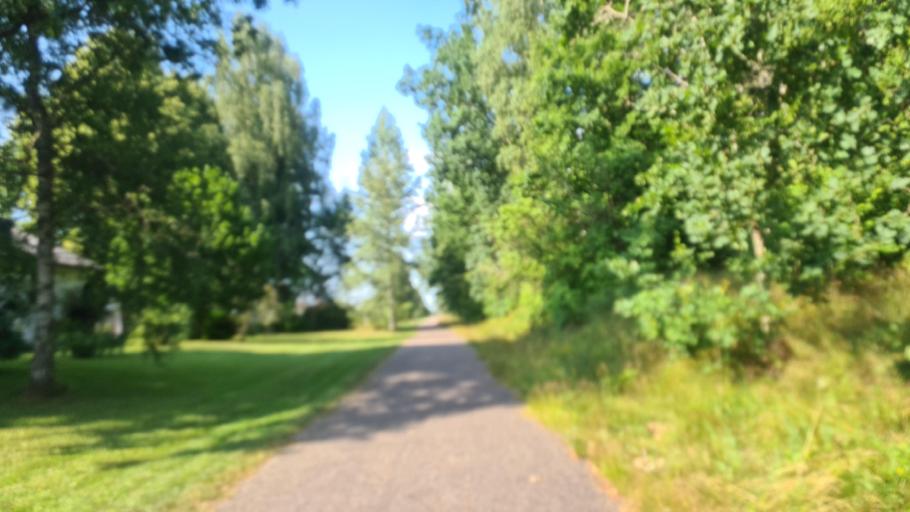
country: SE
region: Kronoberg
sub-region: Ljungby Kommun
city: Ljungby
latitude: 56.7807
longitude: 13.9036
